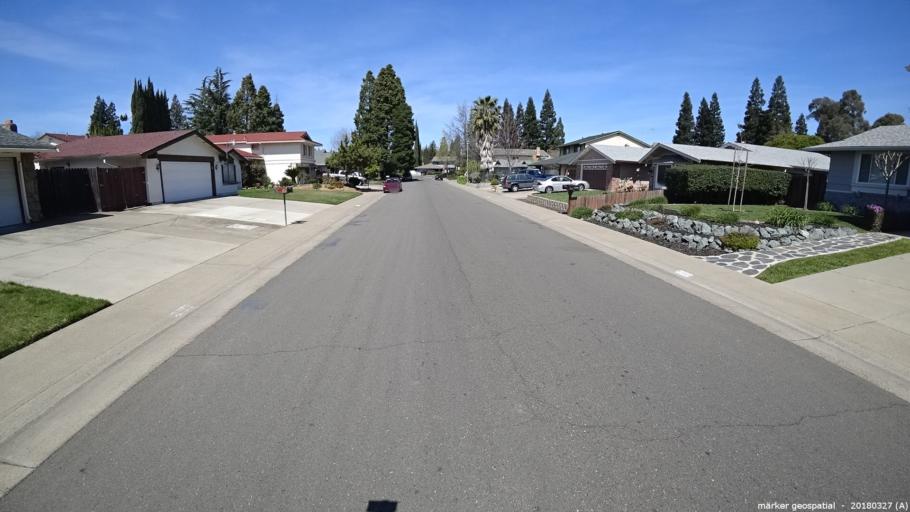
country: US
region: California
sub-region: Sacramento County
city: La Riviera
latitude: 38.5588
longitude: -121.3484
